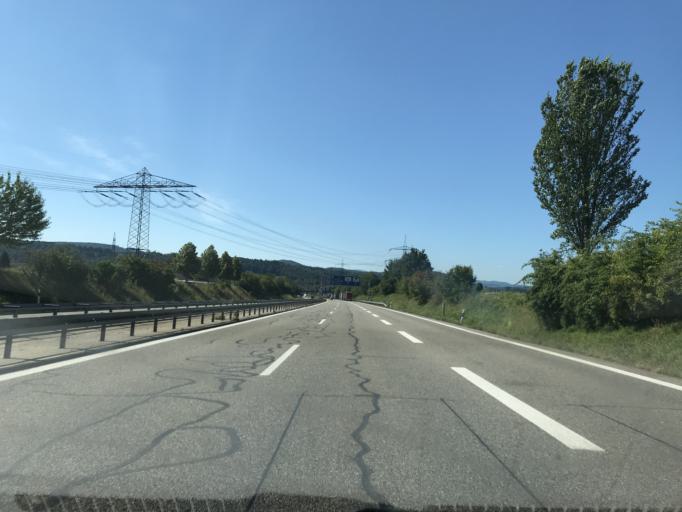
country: DE
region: Baden-Wuerttemberg
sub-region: Freiburg Region
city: Rheinfelden (Baden)
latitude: 47.5600
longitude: 7.7580
